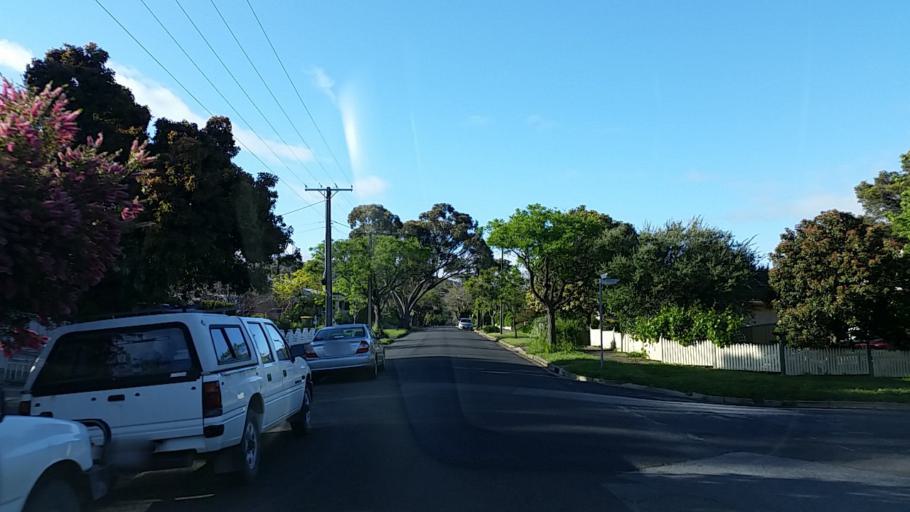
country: AU
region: South Australia
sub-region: Mitcham
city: Clapham
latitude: -34.9871
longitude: 138.6036
